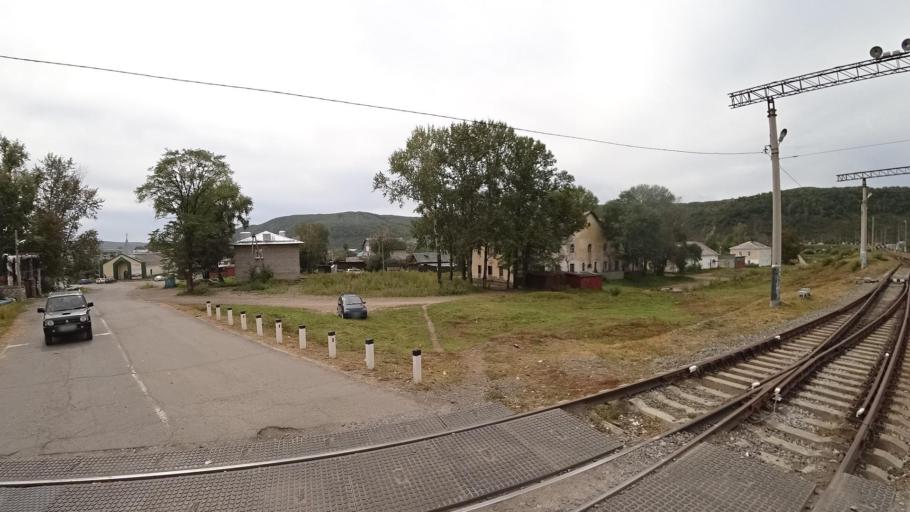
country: RU
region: Jewish Autonomous Oblast
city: Khingansk
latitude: 49.0169
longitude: 131.0547
